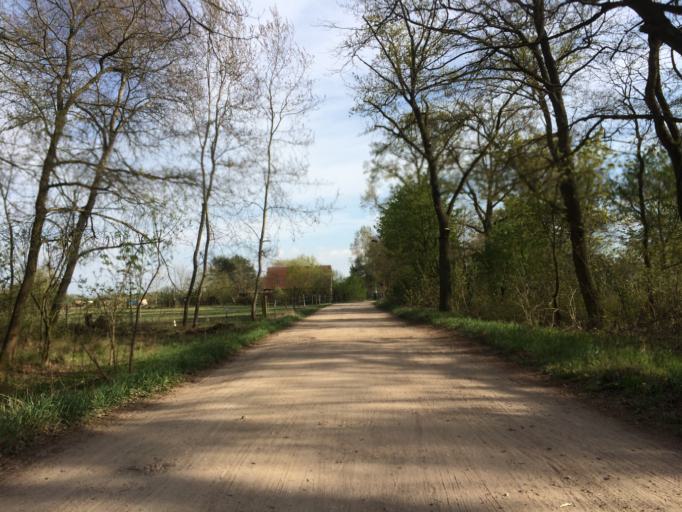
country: DE
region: Berlin
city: Buch
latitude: 52.6815
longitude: 13.4757
